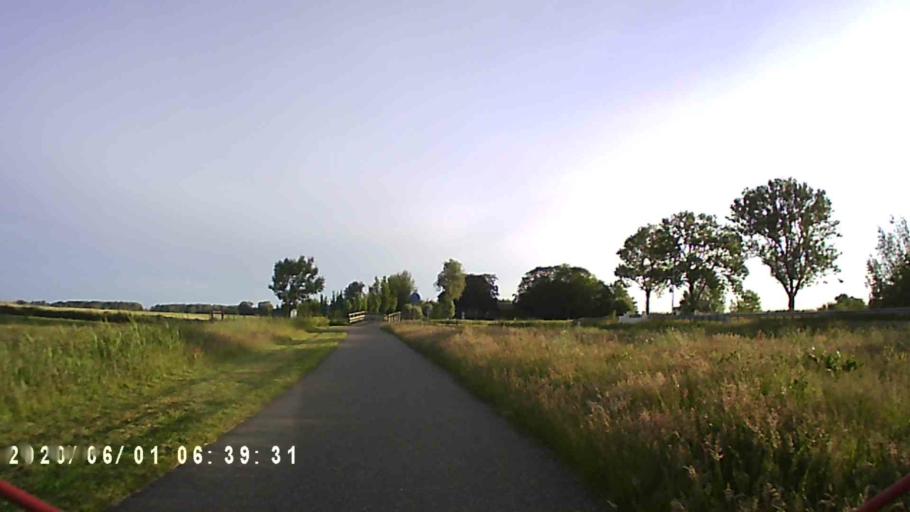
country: NL
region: Friesland
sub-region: Gemeente Kollumerland en Nieuwkruisland
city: Kollum
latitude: 53.2904
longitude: 6.1587
